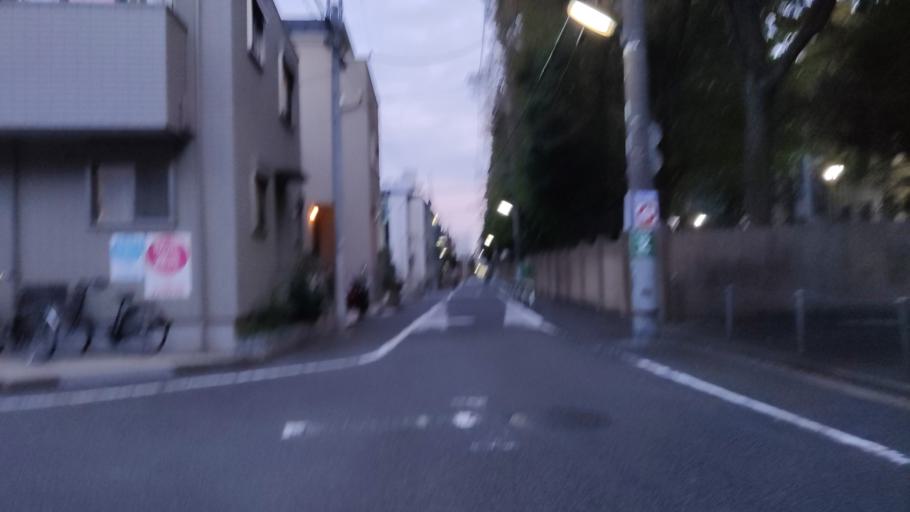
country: JP
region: Tokyo
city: Tokyo
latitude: 35.6353
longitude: 139.6782
